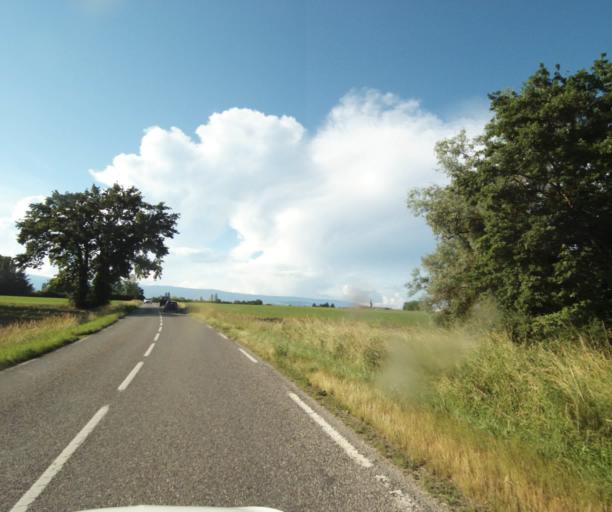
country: FR
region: Rhone-Alpes
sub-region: Departement de la Haute-Savoie
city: Messery
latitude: 46.3446
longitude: 6.2921
